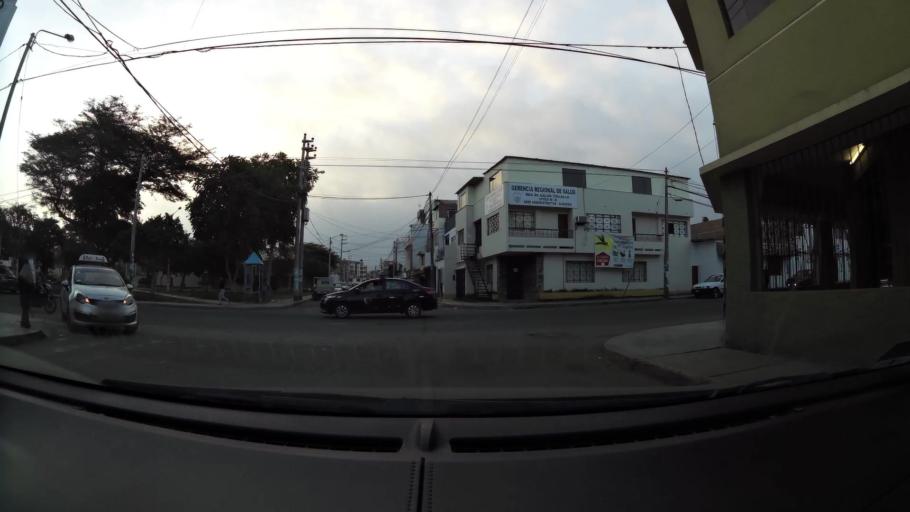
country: PE
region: La Libertad
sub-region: Provincia de Trujillo
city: Trujillo
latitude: -8.1009
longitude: -79.0385
